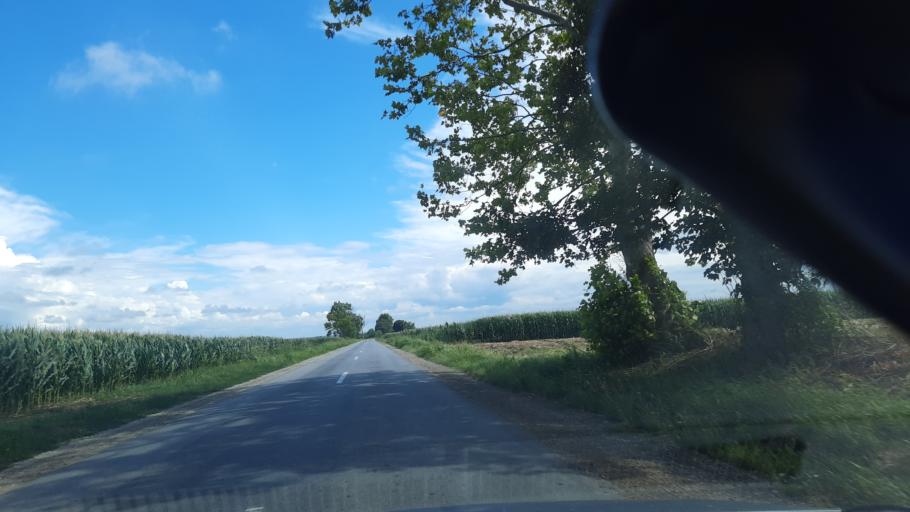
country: RS
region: Autonomna Pokrajina Vojvodina
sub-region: Sremski Okrug
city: Sremska Mitrovica
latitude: 45.0623
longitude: 19.5970
